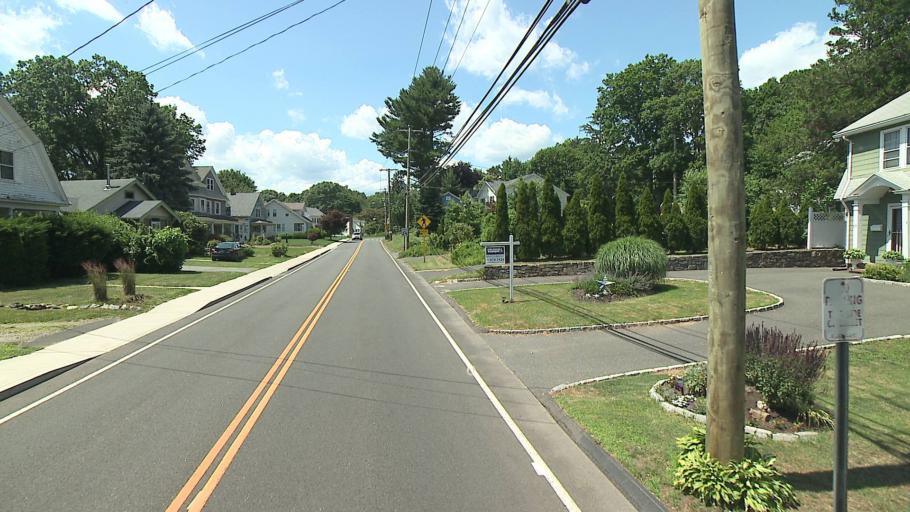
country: US
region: Connecticut
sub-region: New Haven County
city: Milford
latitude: 41.2132
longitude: -73.0611
